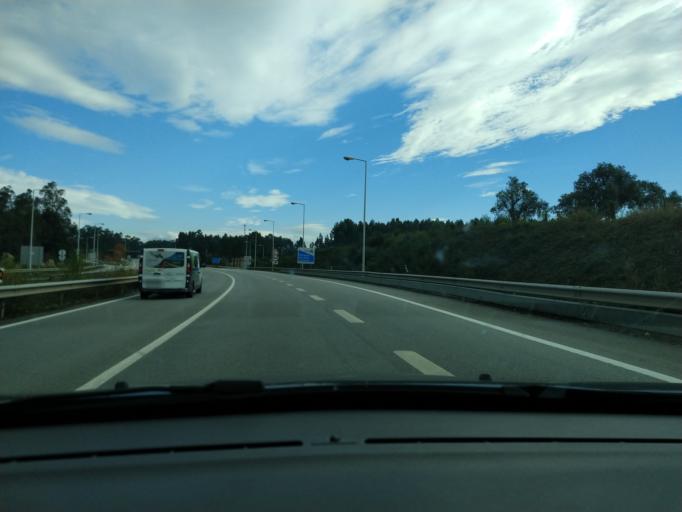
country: PT
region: Aveiro
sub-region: Albergaria-A-Velha
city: Albergaria-a-Velha
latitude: 40.6828
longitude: -8.5282
